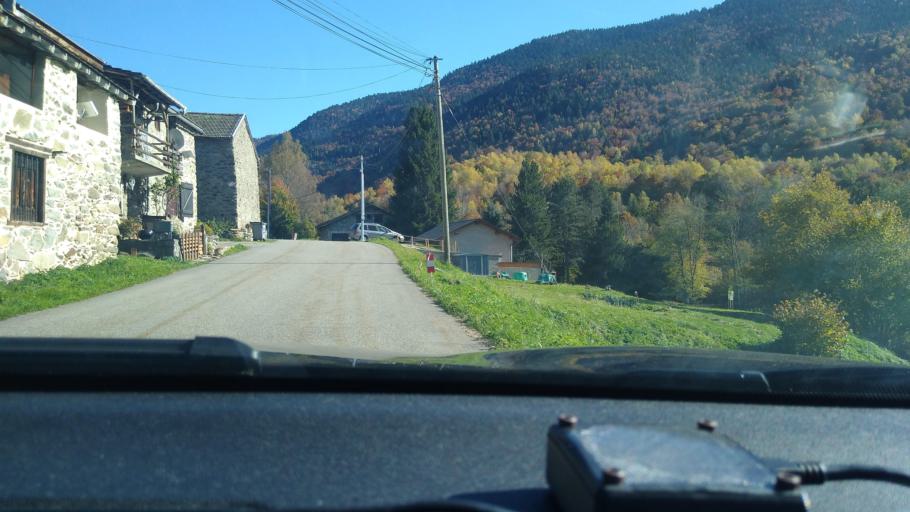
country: FR
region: Midi-Pyrenees
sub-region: Departement de l'Ariege
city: Ax-les-Thermes
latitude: 42.7235
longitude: 1.8976
